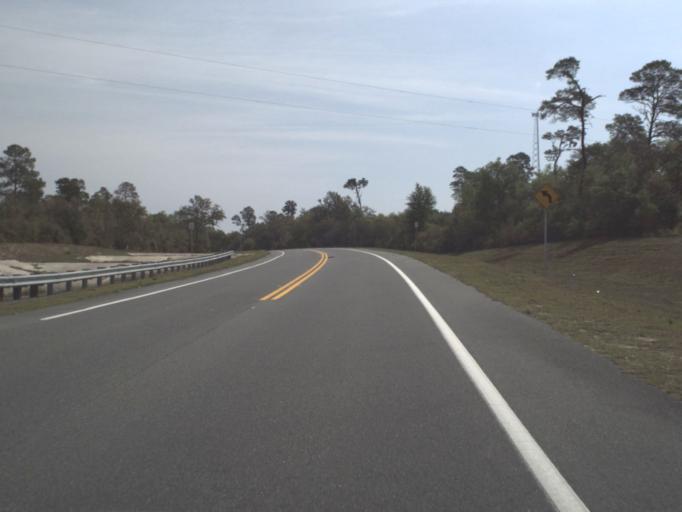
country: US
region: Florida
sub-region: Lake County
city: Astor
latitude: 29.2141
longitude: -81.6526
